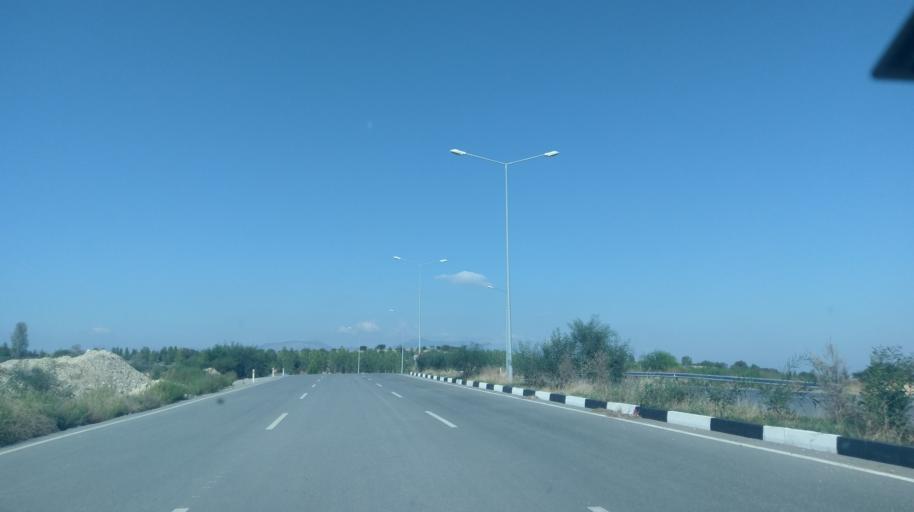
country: CY
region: Larnaka
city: Athienou
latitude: 35.1525
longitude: 33.5195
